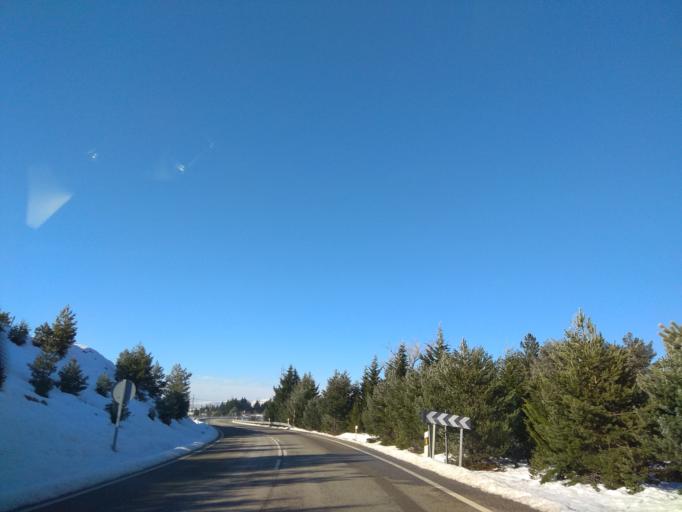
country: ES
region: Castille and Leon
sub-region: Provincia de Burgos
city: Arija
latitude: 42.9986
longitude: -3.8384
